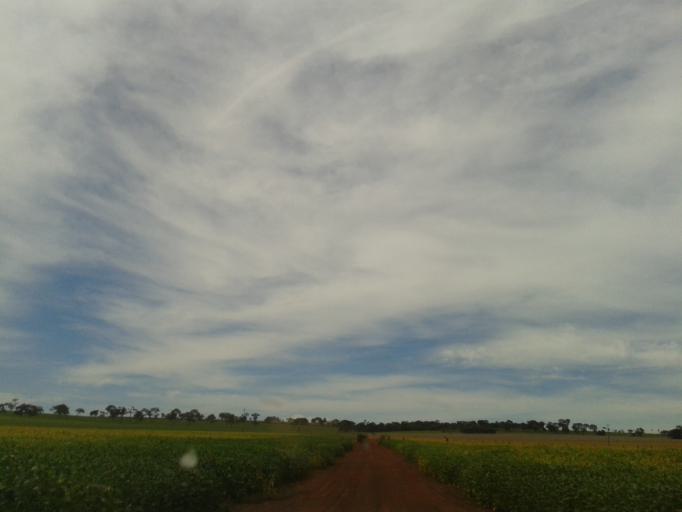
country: BR
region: Minas Gerais
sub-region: Capinopolis
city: Capinopolis
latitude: -18.7680
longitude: -49.7966
